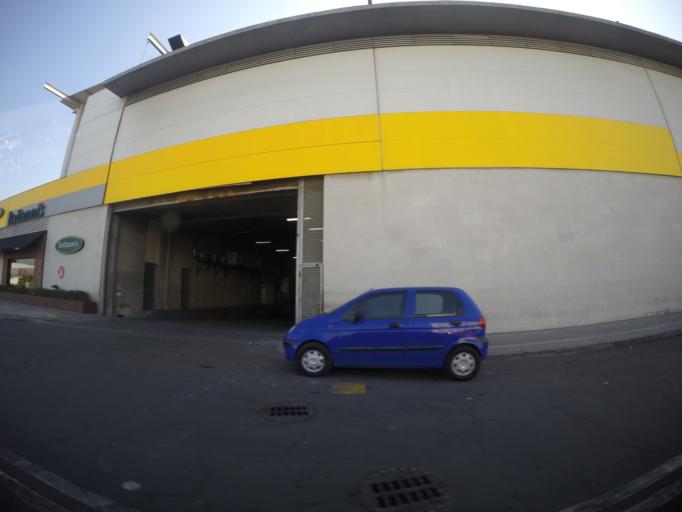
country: MX
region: Mexico
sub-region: Atenco
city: Colonia el Salado
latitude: 19.5837
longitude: -99.0240
